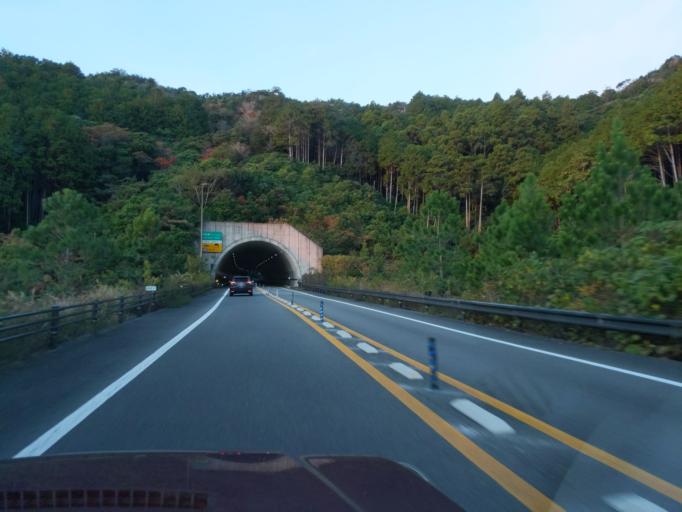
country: JP
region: Tokushima
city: Anan
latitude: 33.7715
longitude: 134.5759
